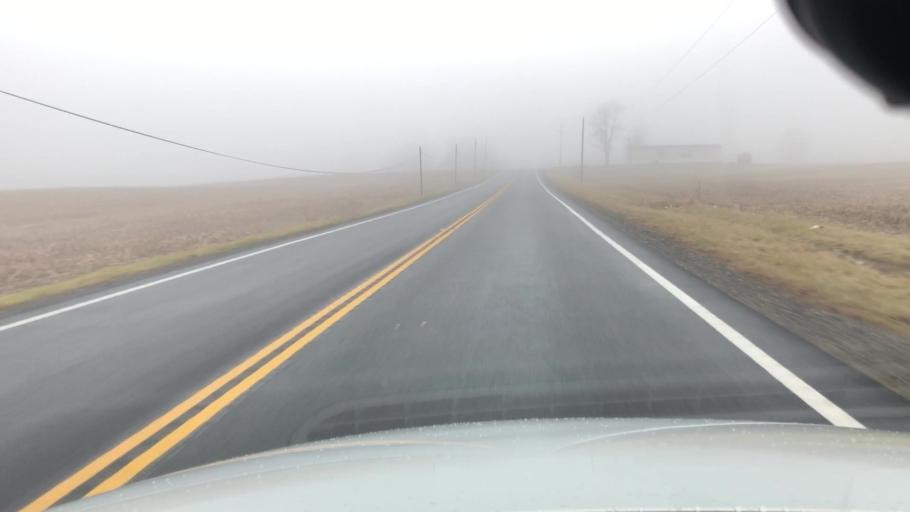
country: US
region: Ohio
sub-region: Logan County
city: Lakeview
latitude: 40.5962
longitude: -83.8684
